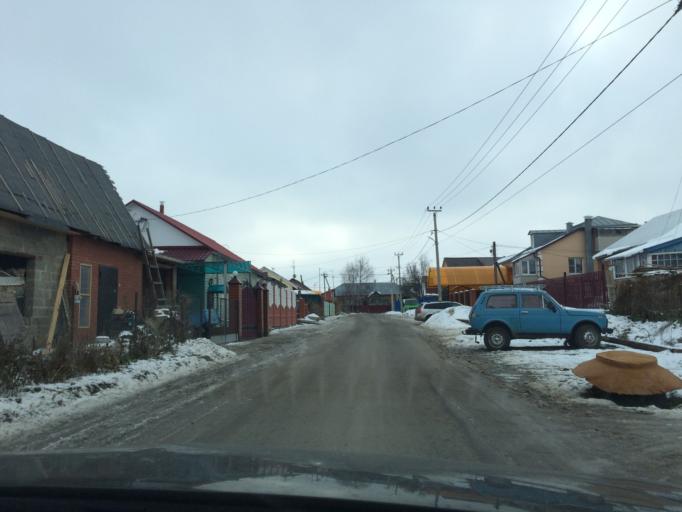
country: RU
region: Tula
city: Plavsk
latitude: 53.7075
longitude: 37.2978
